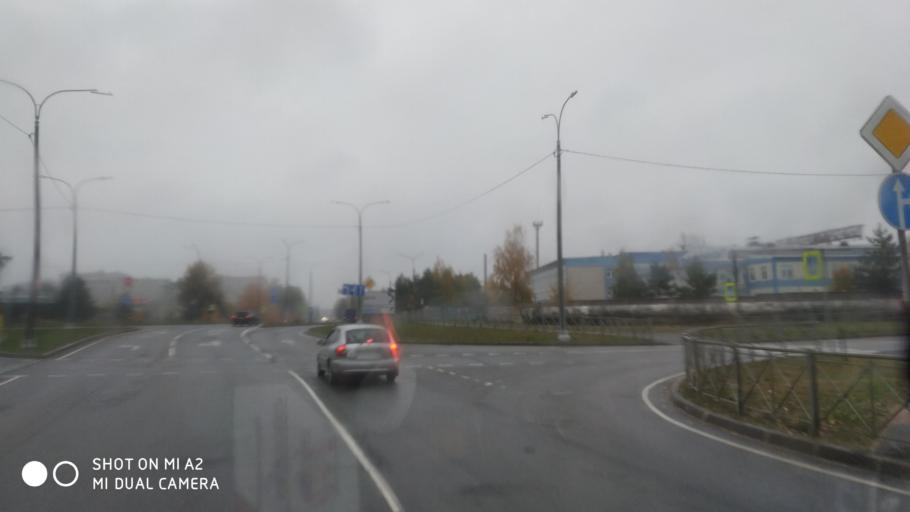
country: RU
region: Leningrad
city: Sosnovyy Bor
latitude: 59.8831
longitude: 29.0969
